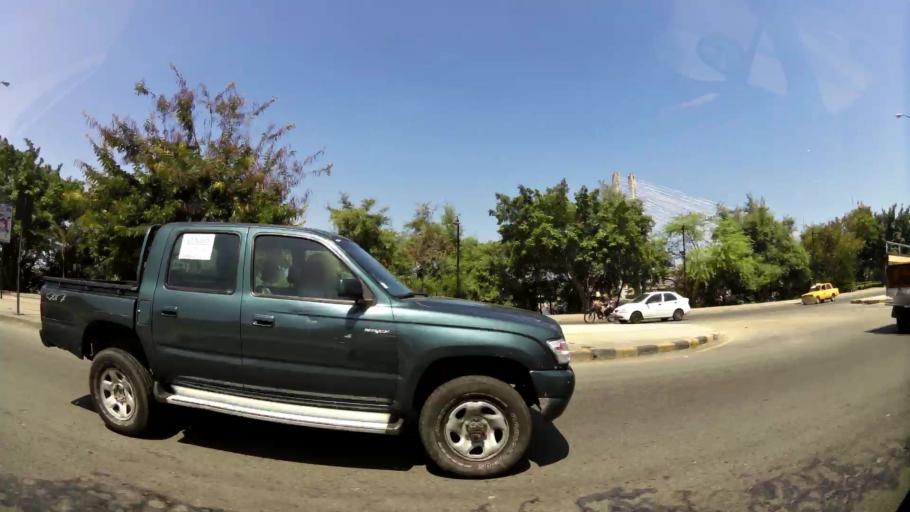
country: EC
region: Guayas
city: Guayaquil
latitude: -2.1883
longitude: -79.9251
